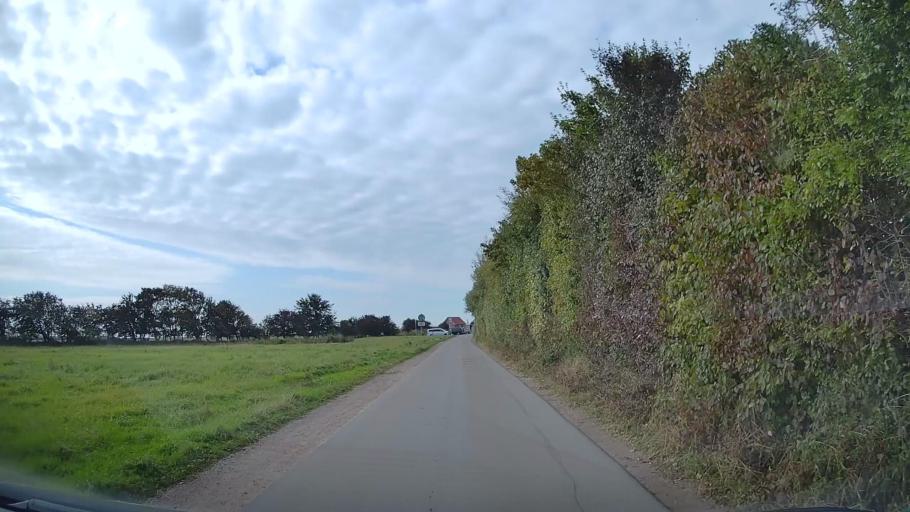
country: DE
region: Schleswig-Holstein
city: Grossenbrode
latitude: 54.5230
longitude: 11.0506
